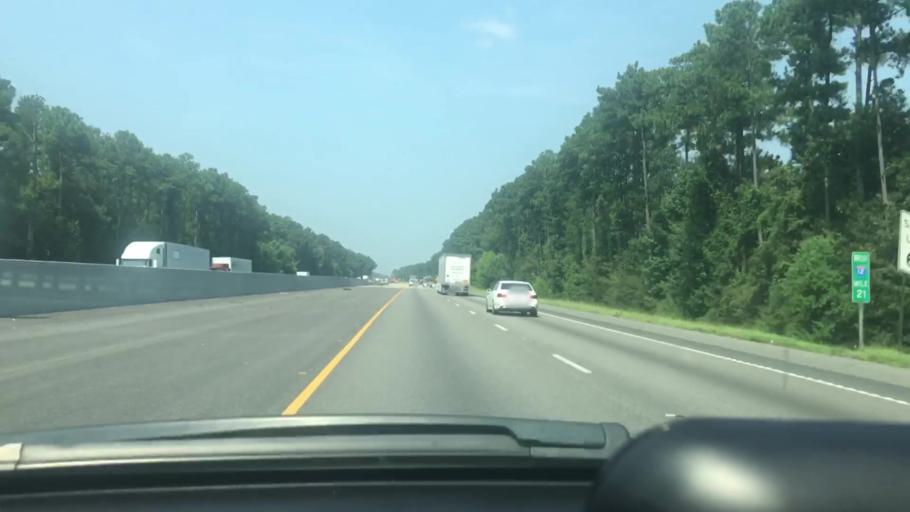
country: US
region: Louisiana
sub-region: Livingston Parish
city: Livingston
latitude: 30.4741
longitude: -90.7784
